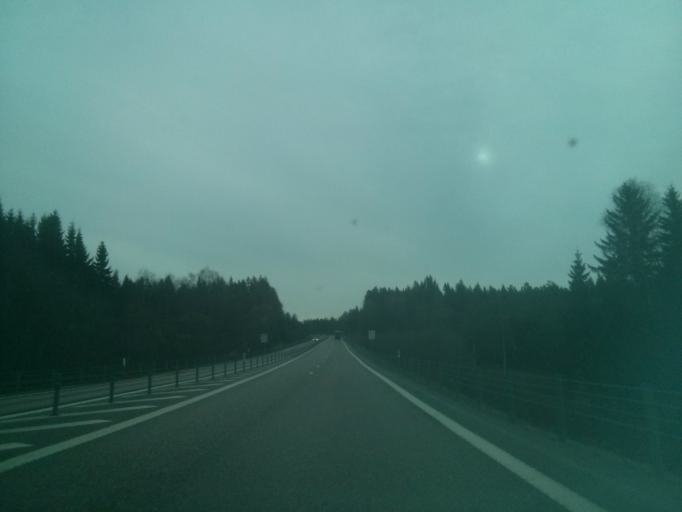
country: SE
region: Vaesternorrland
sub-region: Timra Kommun
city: Soraker
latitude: 62.5621
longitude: 17.7143
